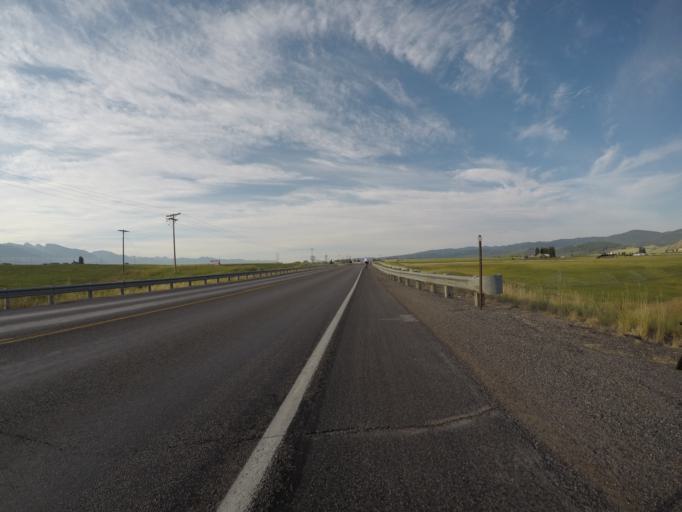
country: US
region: Wyoming
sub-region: Lincoln County
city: Afton
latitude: 42.9862
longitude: -111.0124
